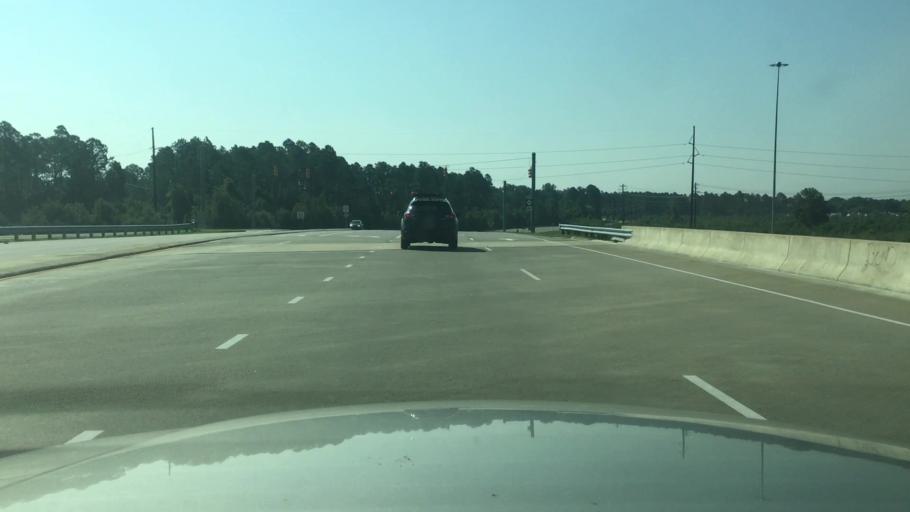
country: US
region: North Carolina
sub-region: Cumberland County
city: Spring Lake
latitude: 35.1396
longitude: -78.9063
